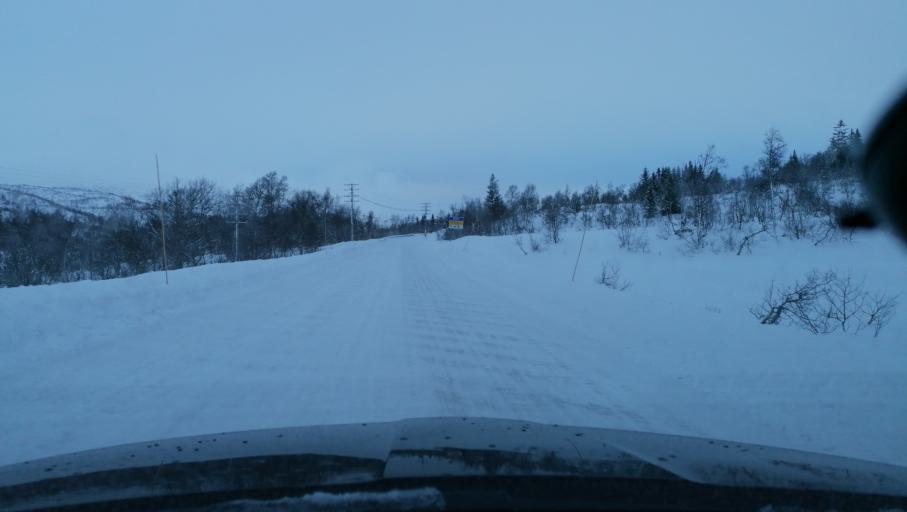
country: NO
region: Aust-Agder
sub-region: Bykle
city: Hovden
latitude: 59.6373
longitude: 7.4538
